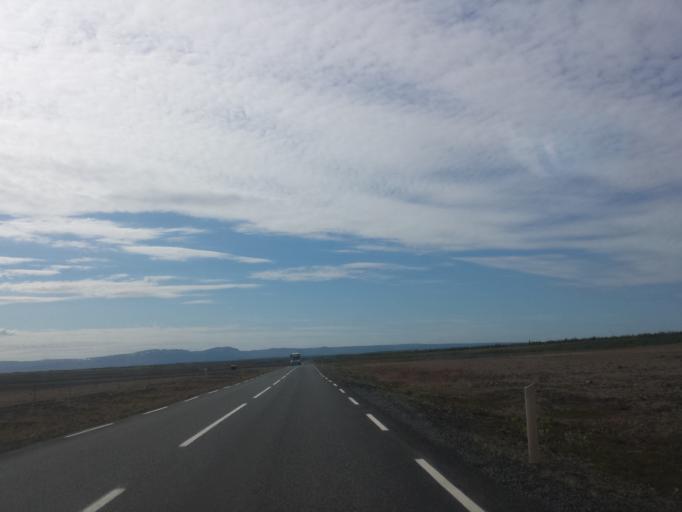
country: IS
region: Northeast
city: Husavik
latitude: 66.0319
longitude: -16.5164
